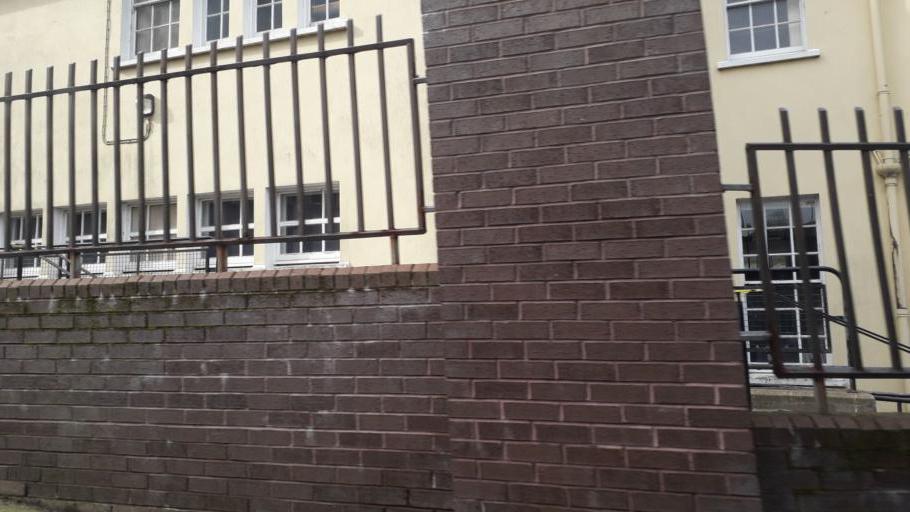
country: IE
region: Munster
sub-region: County Cork
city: Cork
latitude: 51.8932
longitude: -8.4949
